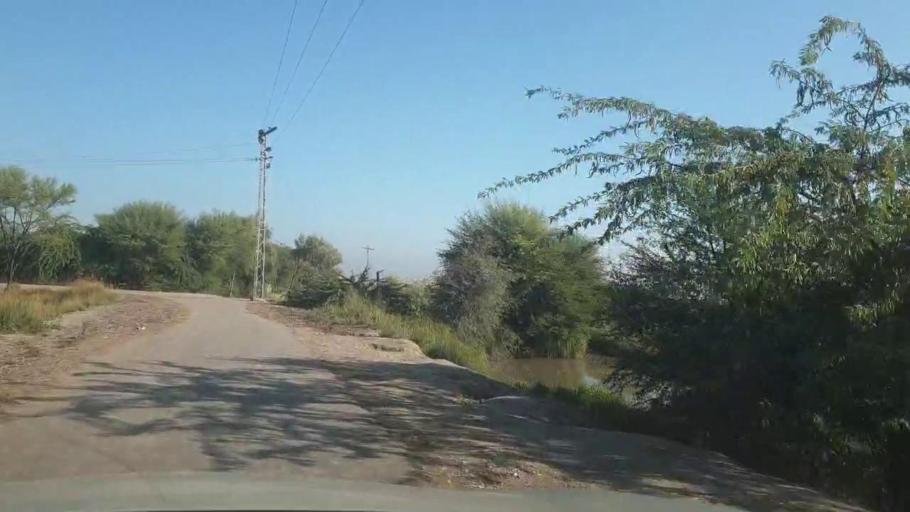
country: PK
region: Sindh
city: Bhan
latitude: 26.5468
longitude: 67.6907
